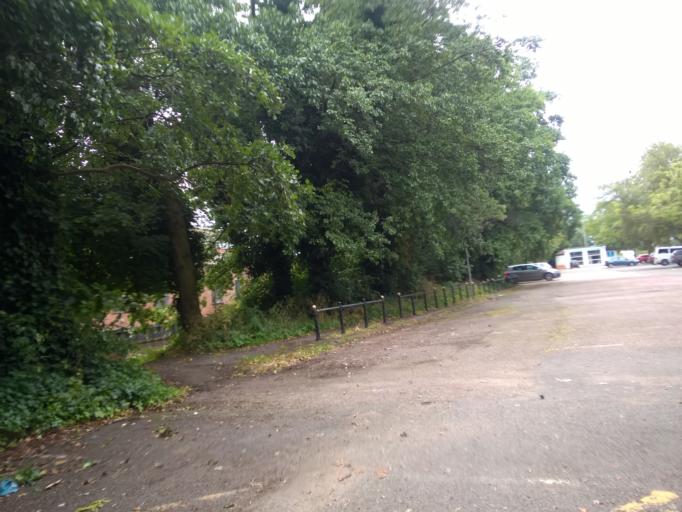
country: GB
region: England
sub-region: City of Leicester
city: Leicester
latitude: 52.6430
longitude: -1.1372
